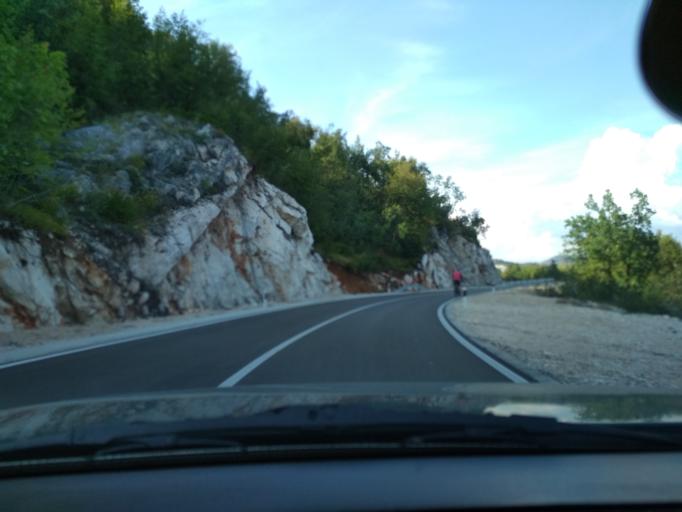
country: ME
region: Cetinje
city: Cetinje
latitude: 42.4206
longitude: 18.8743
